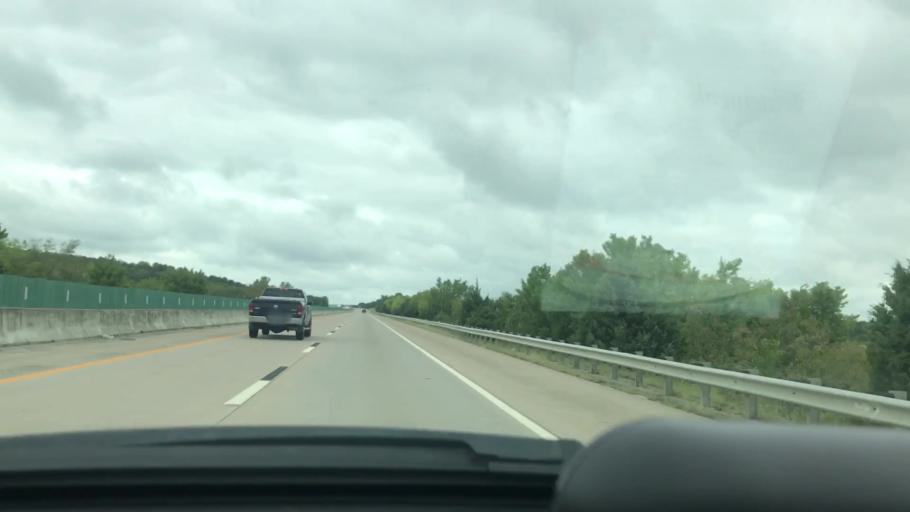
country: US
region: Oklahoma
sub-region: Pittsburg County
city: Krebs
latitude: 35.0261
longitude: -95.7153
